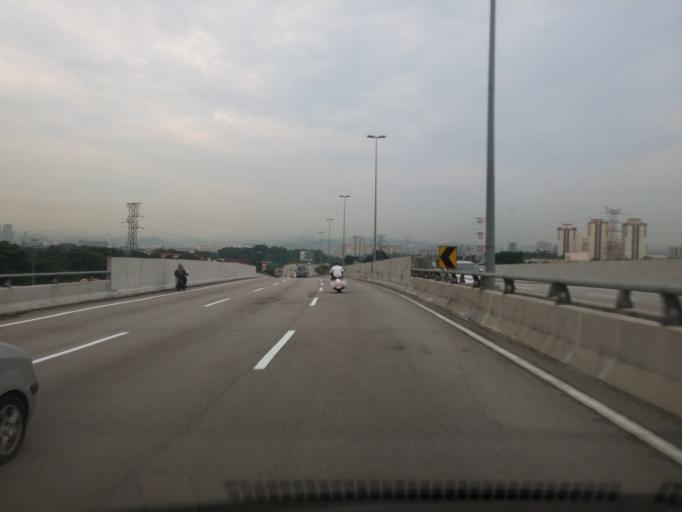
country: MY
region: Kuala Lumpur
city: Kuala Lumpur
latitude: 3.1002
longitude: 101.7022
